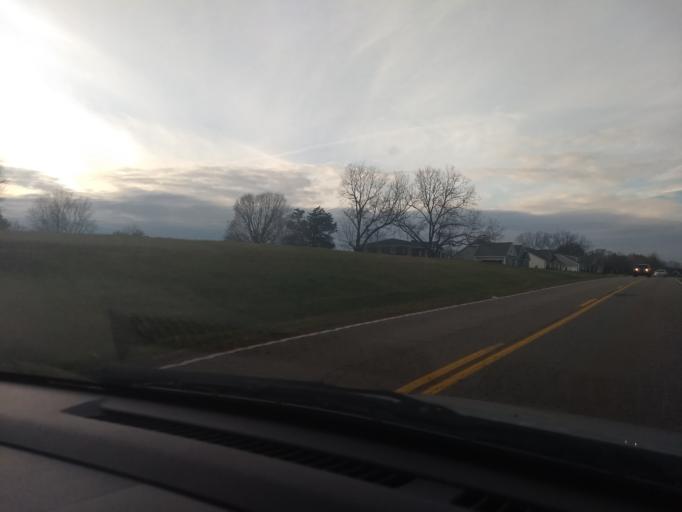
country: US
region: South Carolina
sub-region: Greenville County
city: Greer
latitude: 34.9828
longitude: -82.1987
